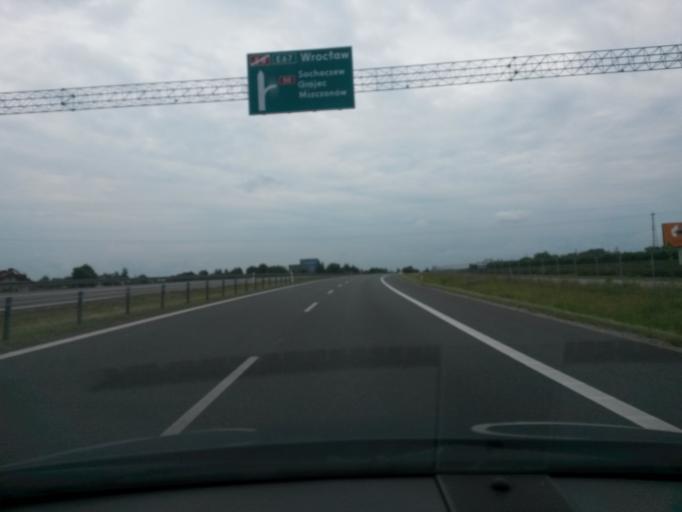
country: PL
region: Masovian Voivodeship
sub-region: Powiat zyrardowski
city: Mszczonow
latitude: 51.9855
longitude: 20.5343
